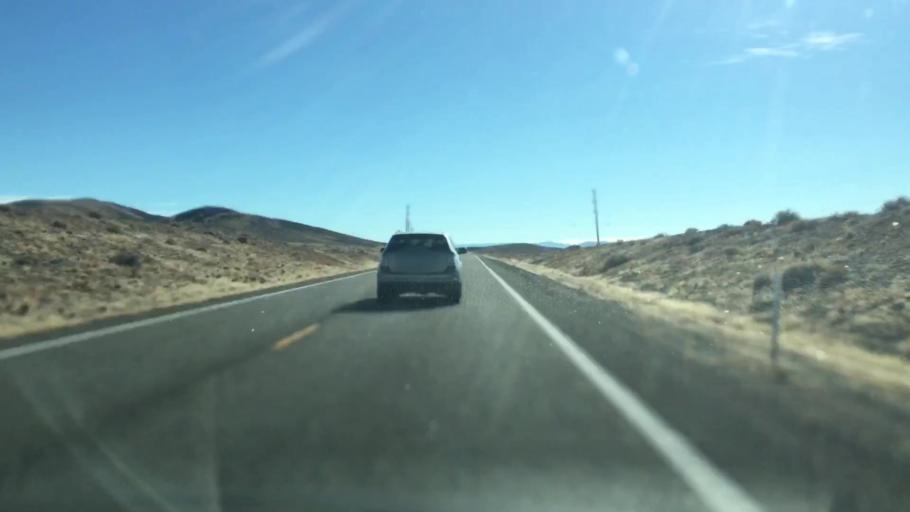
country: US
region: Nevada
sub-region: Lyon County
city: Silver Springs
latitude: 39.1985
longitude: -119.2131
